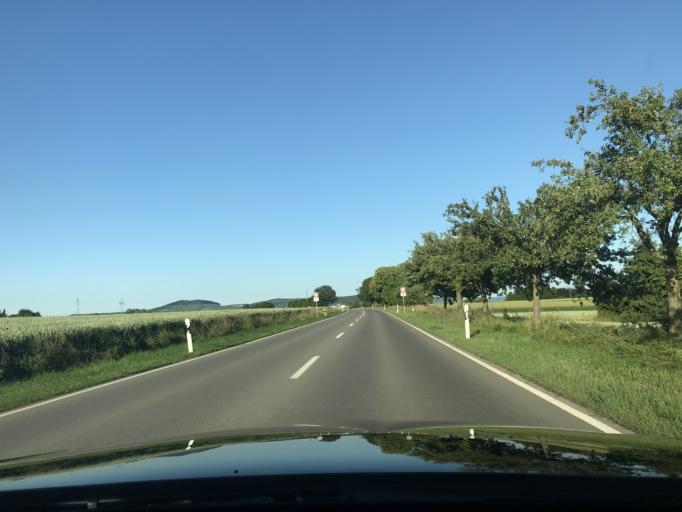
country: DE
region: Baden-Wuerttemberg
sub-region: Regierungsbezirk Stuttgart
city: Fellbach
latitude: 48.8355
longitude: 9.2805
